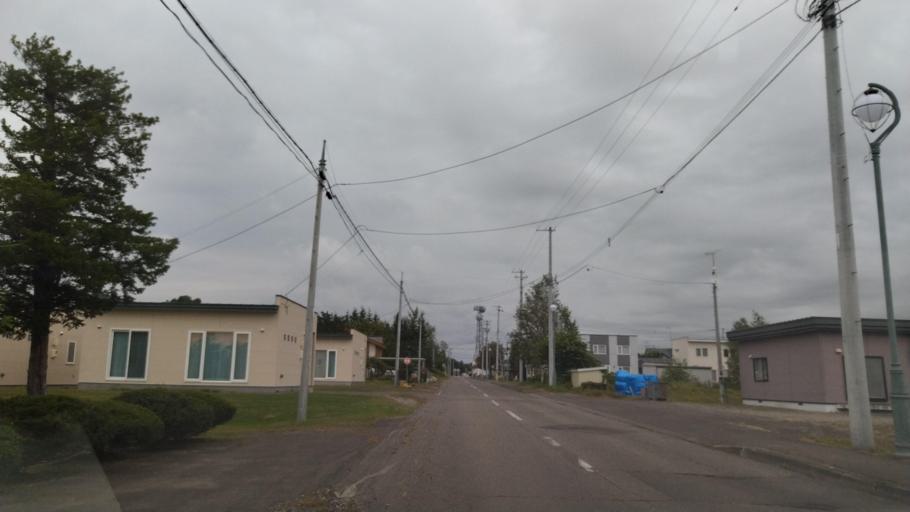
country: JP
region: Hokkaido
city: Otofuke
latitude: 43.2221
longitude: 143.2857
